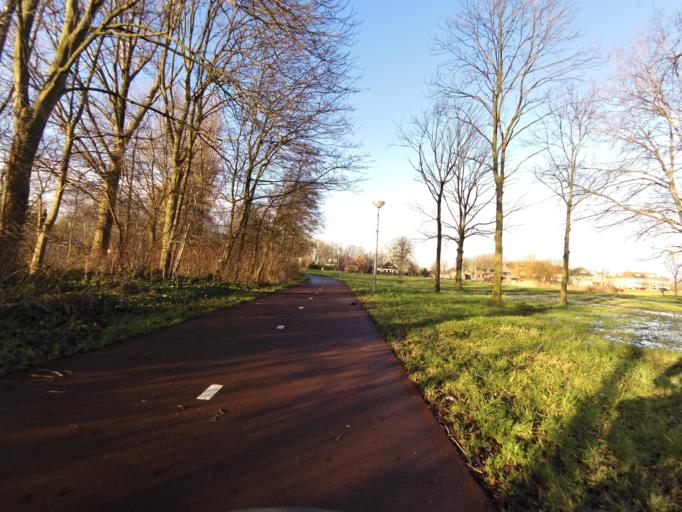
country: NL
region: South Holland
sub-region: Gemeente Rotterdam
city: Delfshaven
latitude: 51.9385
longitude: 4.4493
